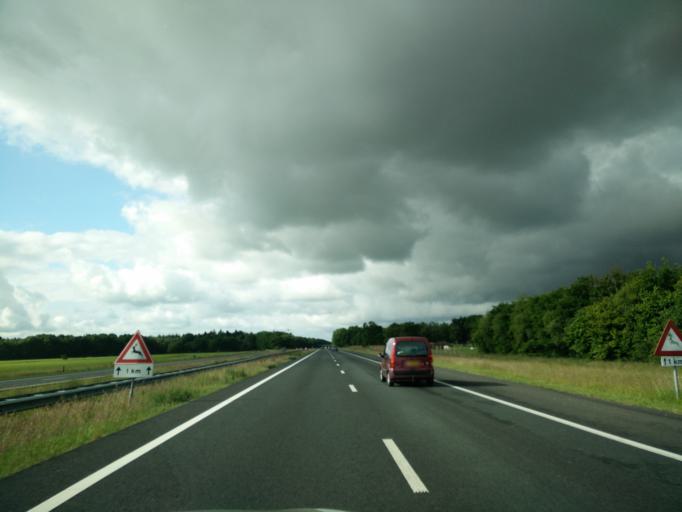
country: NL
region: Drenthe
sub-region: Gemeente Assen
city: Assen
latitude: 52.9340
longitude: 6.5366
